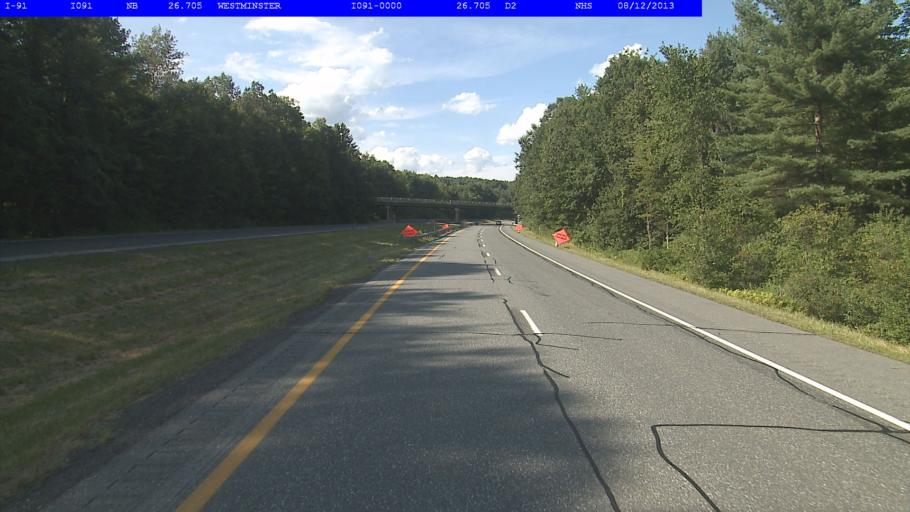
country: US
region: Vermont
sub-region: Windham County
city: Bellows Falls
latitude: 43.0657
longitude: -72.4701
